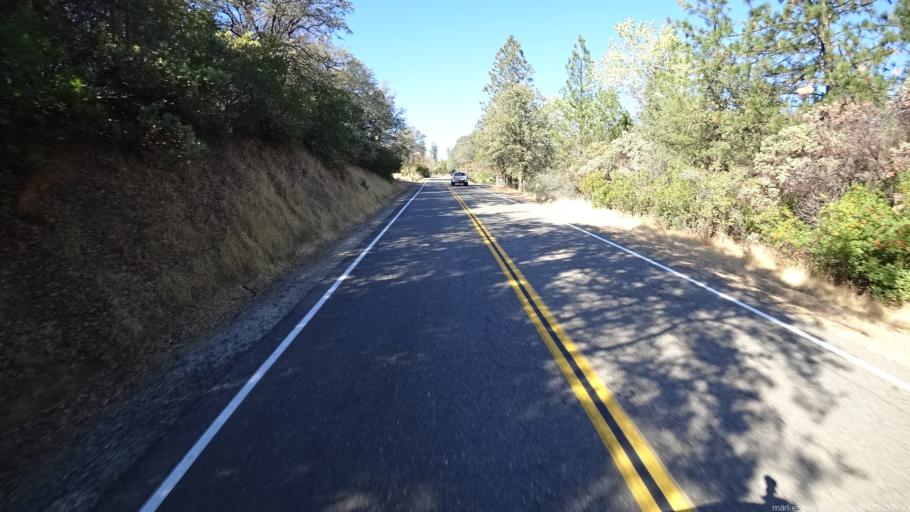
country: US
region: California
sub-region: Shasta County
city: Shasta
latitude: 40.6164
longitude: -122.4614
